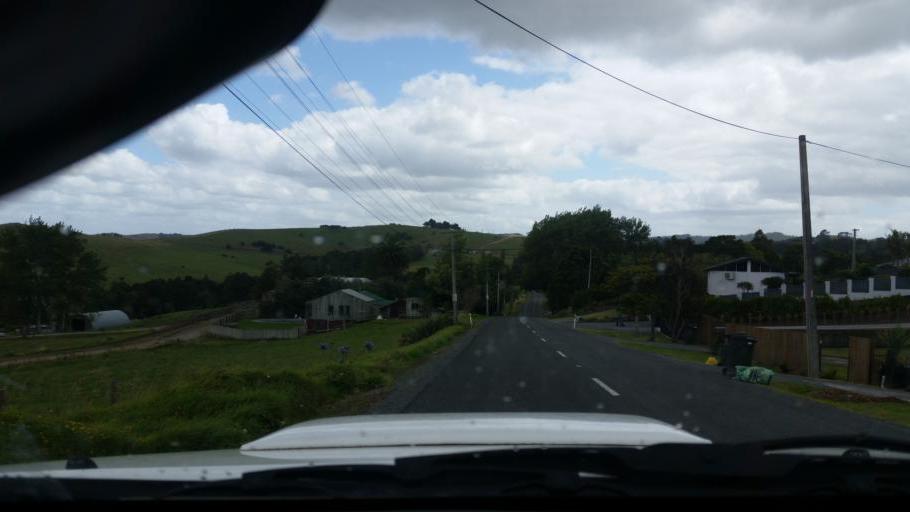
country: NZ
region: Northland
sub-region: Whangarei
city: Ruakaka
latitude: -36.1005
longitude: 174.3509
